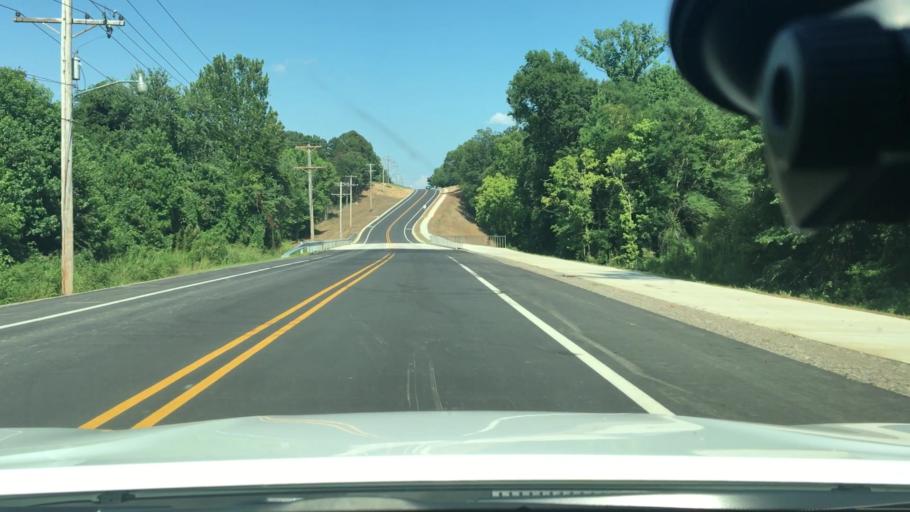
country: US
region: Arkansas
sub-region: Johnson County
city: Clarksville
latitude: 35.4620
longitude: -93.4984
